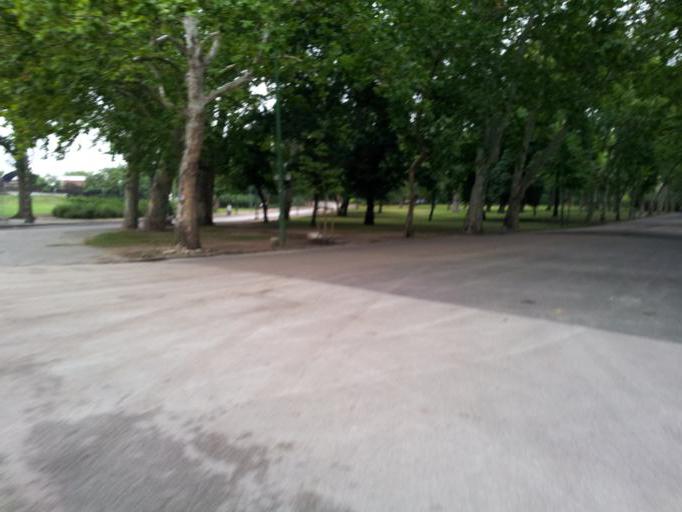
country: HU
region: Budapest
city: Budapest XIII. keruelet
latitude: 47.5121
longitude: 19.0851
